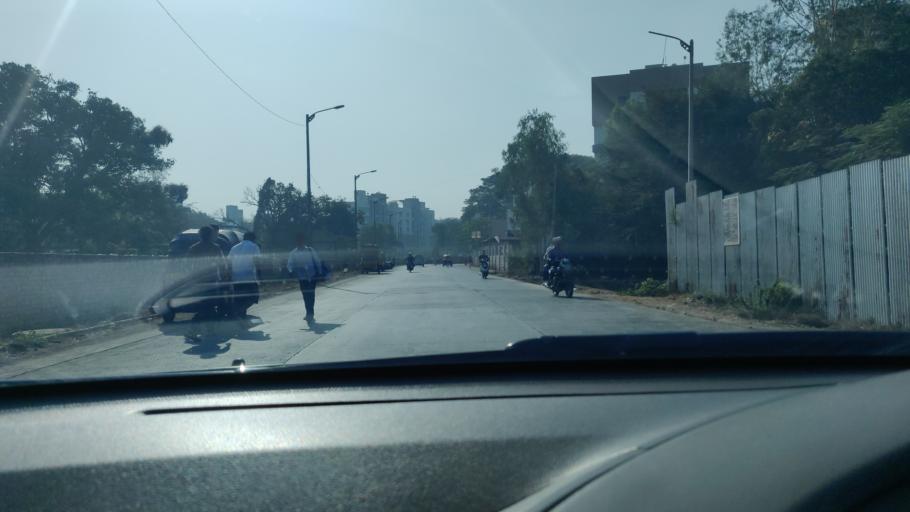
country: IN
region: Maharashtra
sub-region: Pune Division
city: Khadki
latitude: 18.5612
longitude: 73.7923
